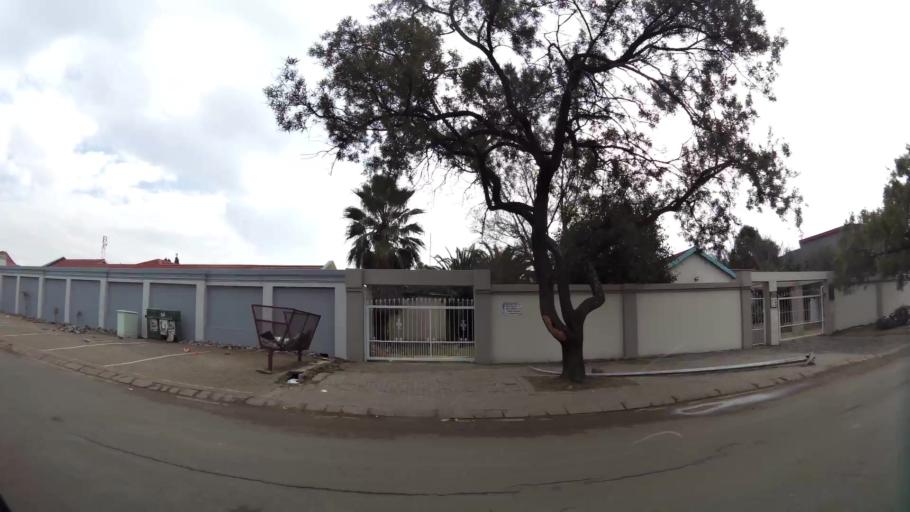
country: ZA
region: Gauteng
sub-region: Sedibeng District Municipality
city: Vanderbijlpark
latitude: -26.7127
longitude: 27.8596
